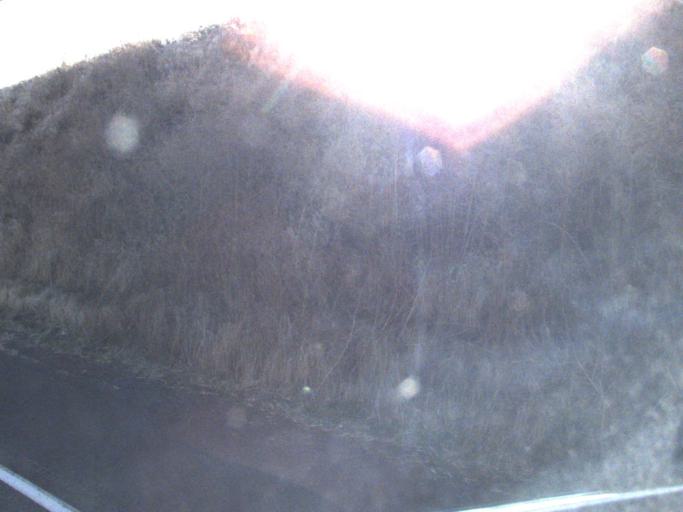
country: US
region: Washington
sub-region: Columbia County
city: Dayton
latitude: 46.3598
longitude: -117.9506
